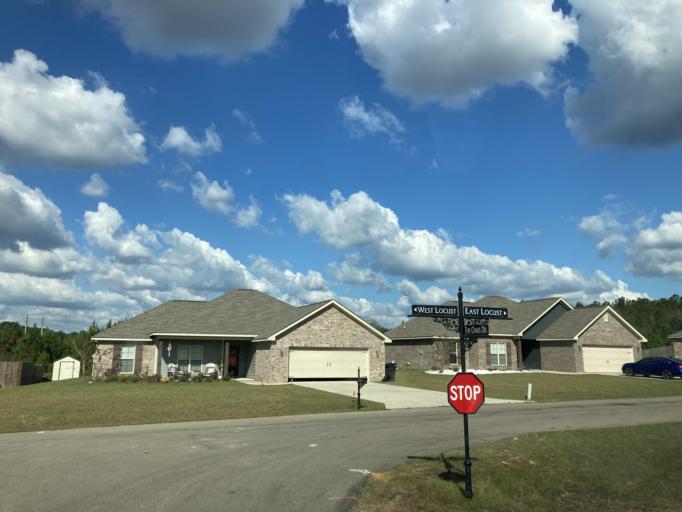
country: US
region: Mississippi
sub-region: Lamar County
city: Sumrall
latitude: 31.4287
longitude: -89.5338
